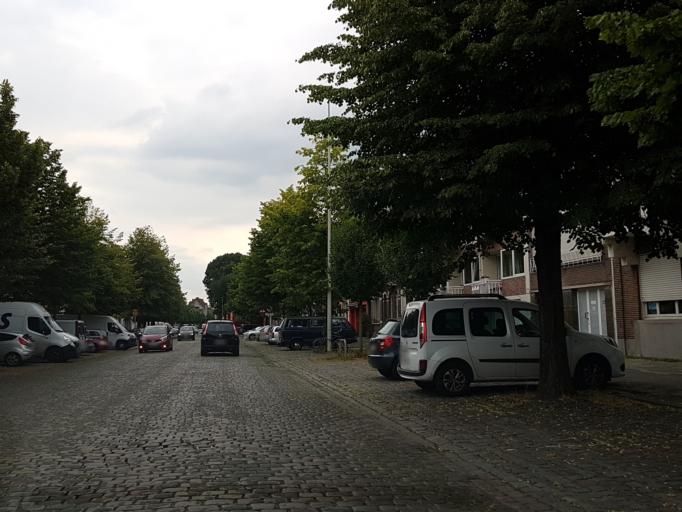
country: BE
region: Flanders
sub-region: Provincie Antwerpen
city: Borsbeek
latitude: 51.1974
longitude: 4.4571
